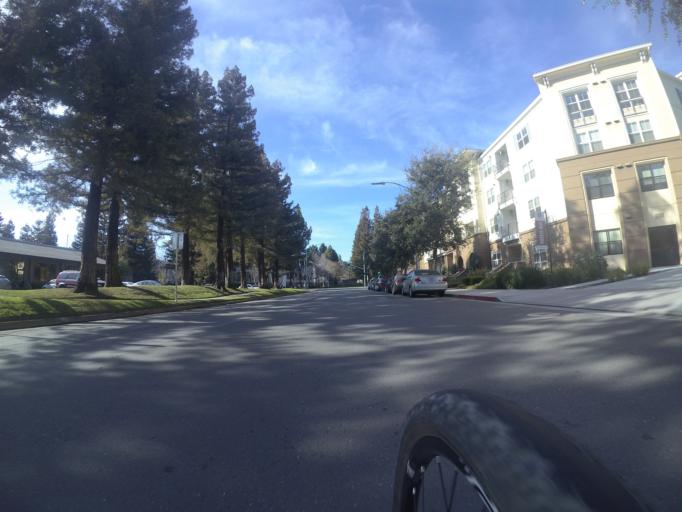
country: US
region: California
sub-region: Santa Clara County
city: Milpitas
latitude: 37.3987
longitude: -121.9212
